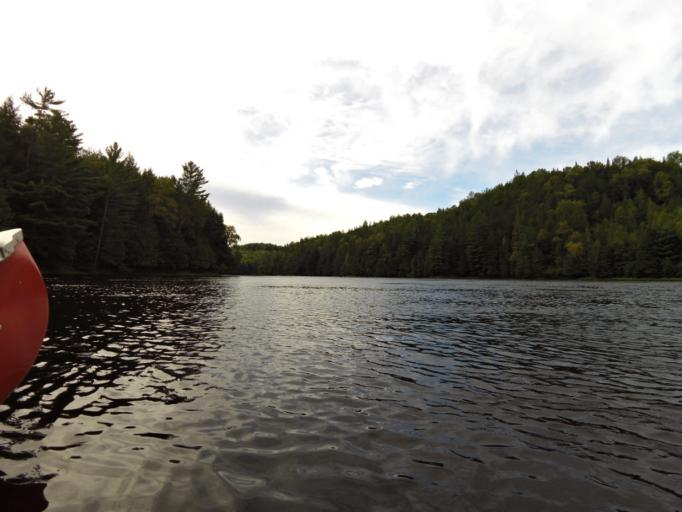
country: CA
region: Quebec
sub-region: Outaouais
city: Wakefield
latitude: 45.7998
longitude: -75.9313
